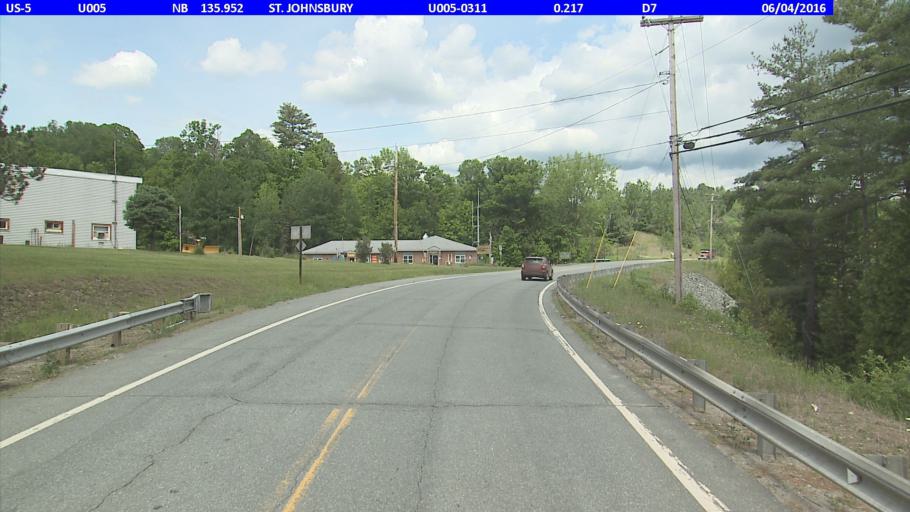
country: US
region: Vermont
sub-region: Caledonia County
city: Saint Johnsbury
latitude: 44.3977
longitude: -72.0247
